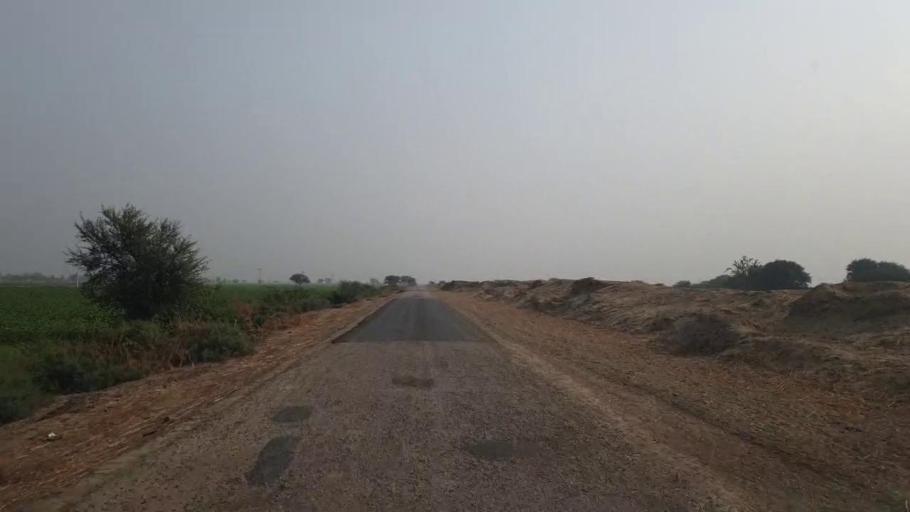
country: PK
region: Sindh
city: Mirpur Batoro
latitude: 24.5785
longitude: 68.3966
